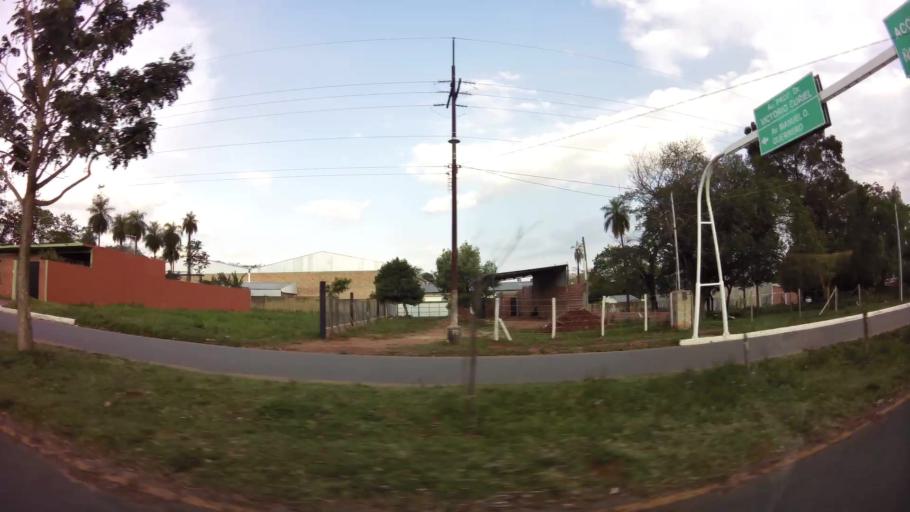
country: PY
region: Central
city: Nemby
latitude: -25.3699
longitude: -57.5247
